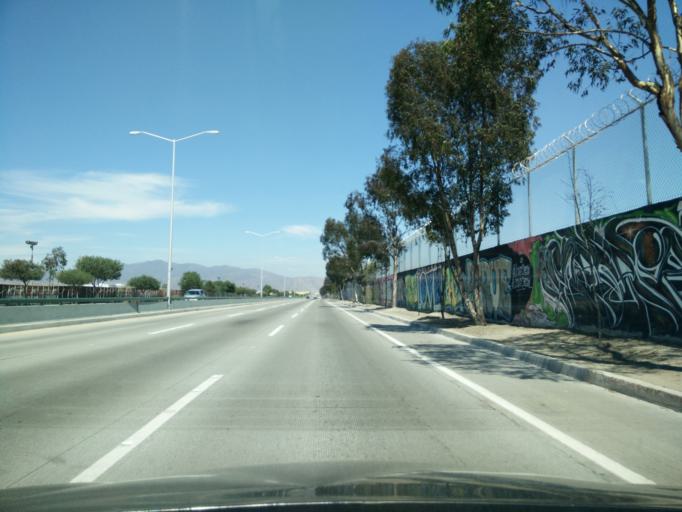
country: MX
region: Baja California
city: Tijuana
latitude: 32.5454
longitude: -116.9922
